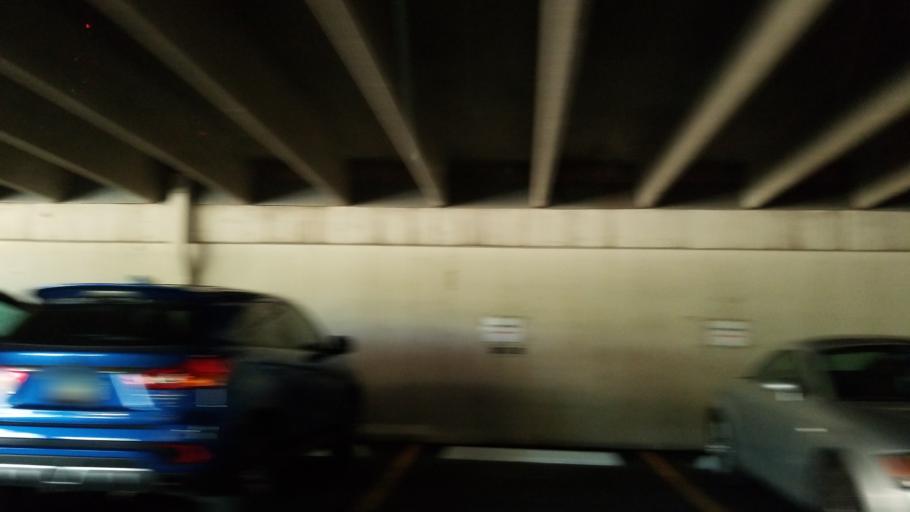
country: US
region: Arizona
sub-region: Maricopa County
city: Phoenix
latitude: 33.4753
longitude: -112.0745
